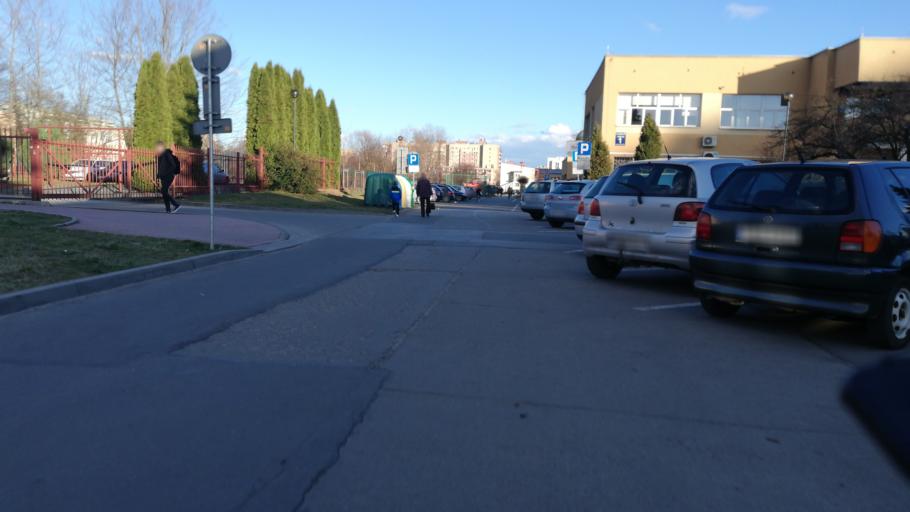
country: PL
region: Lesser Poland Voivodeship
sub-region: Krakow
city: Krakow
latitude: 50.0825
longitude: 20.0041
